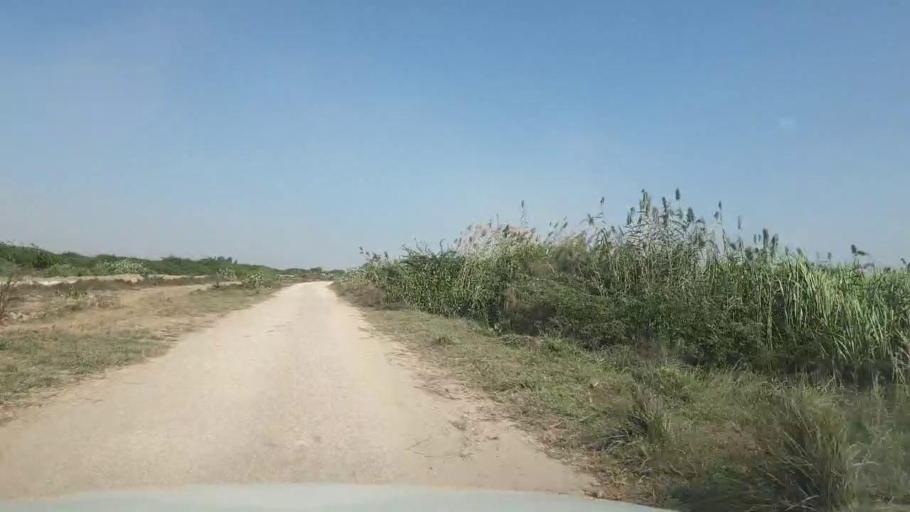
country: PK
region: Sindh
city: Mirpur Sakro
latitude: 24.4078
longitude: 67.7554
